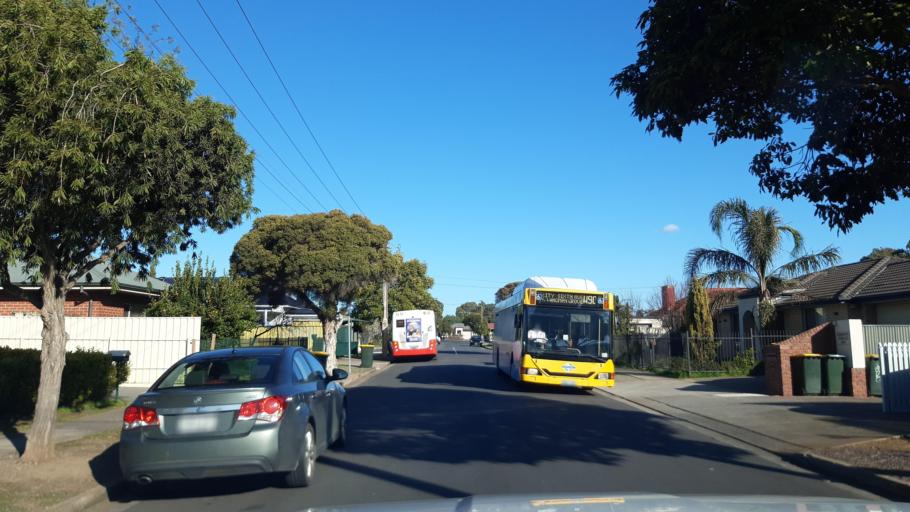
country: AU
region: South Australia
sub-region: Marion
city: Clovelly Park
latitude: -34.9958
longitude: 138.5673
